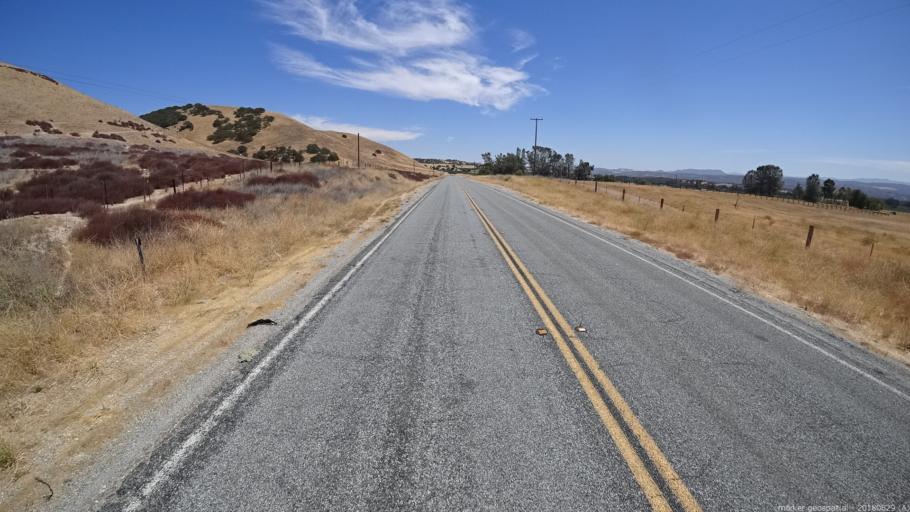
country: US
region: California
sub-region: San Luis Obispo County
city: Lake Nacimiento
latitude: 35.9154
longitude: -121.0264
